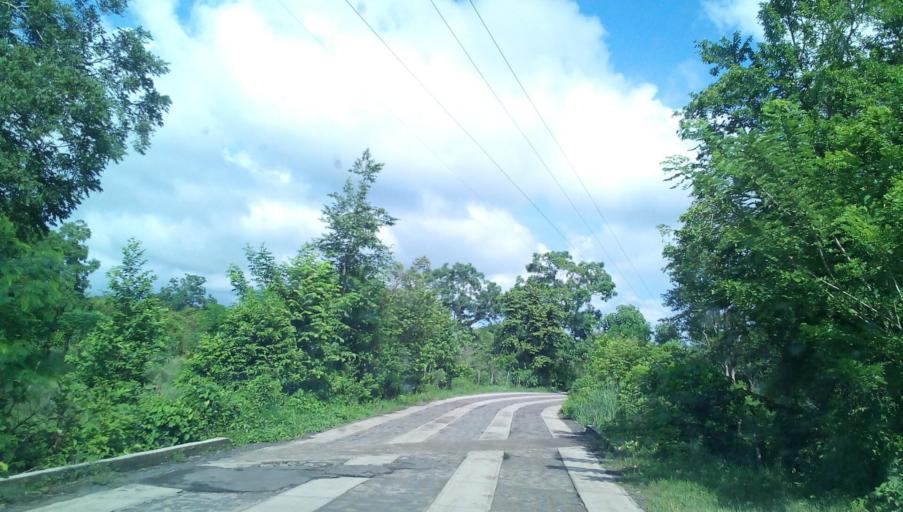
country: MX
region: Veracruz
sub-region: Citlaltepetl
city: Las Sabinas
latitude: 21.3478
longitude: -97.8936
